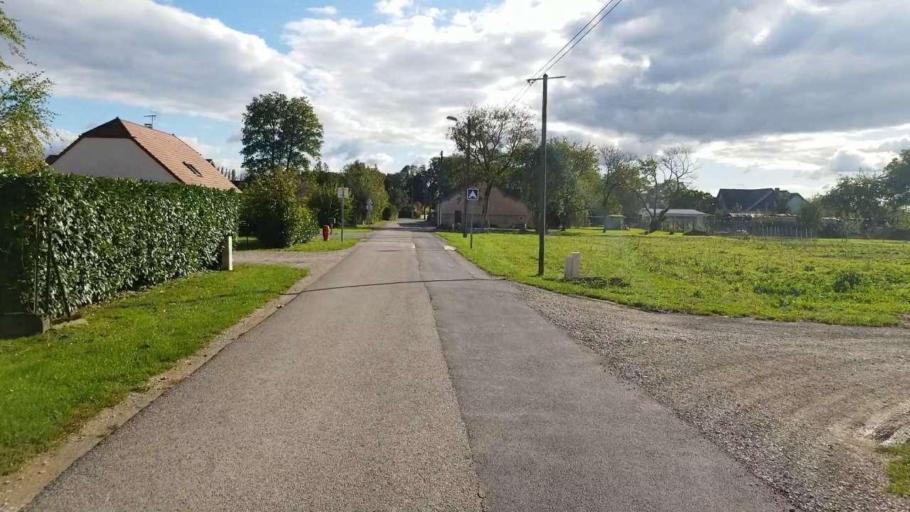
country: FR
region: Franche-Comte
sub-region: Departement du Jura
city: Bletterans
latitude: 46.7385
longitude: 5.4604
